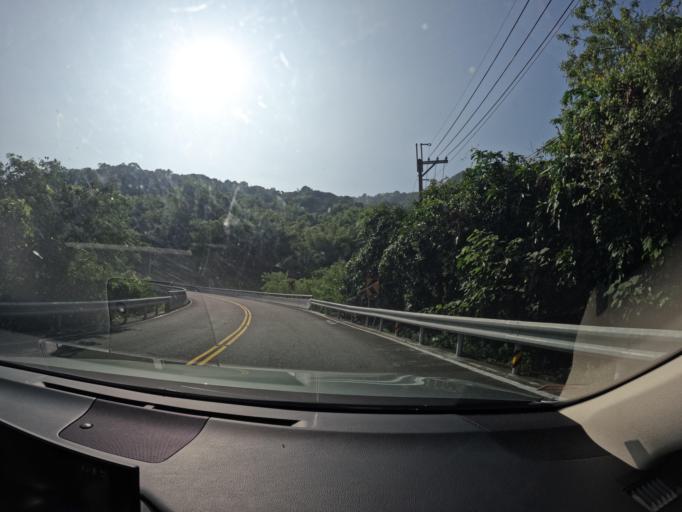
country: TW
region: Taiwan
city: Yujing
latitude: 23.0719
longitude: 120.5417
